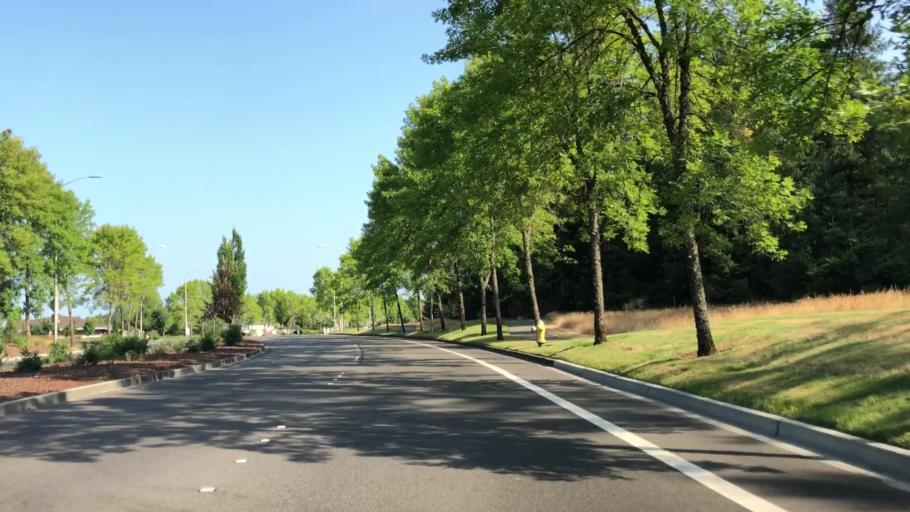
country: US
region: Washington
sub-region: Thurston County
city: Tanglewilde-Thompson Place
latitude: 47.0785
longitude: -122.7520
